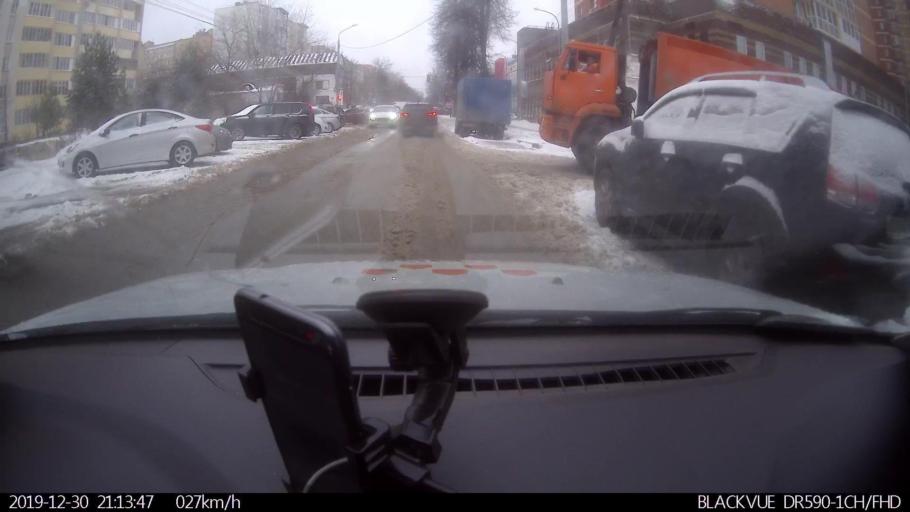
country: RU
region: Nizjnij Novgorod
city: Nizhniy Novgorod
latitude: 56.3118
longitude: 44.0287
